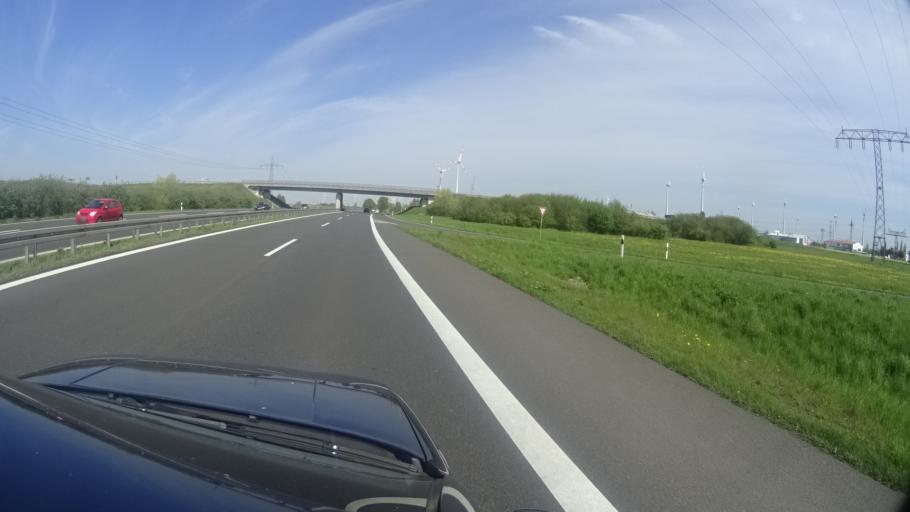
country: DE
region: Brandenburg
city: Wustermark
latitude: 52.5589
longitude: 12.9283
